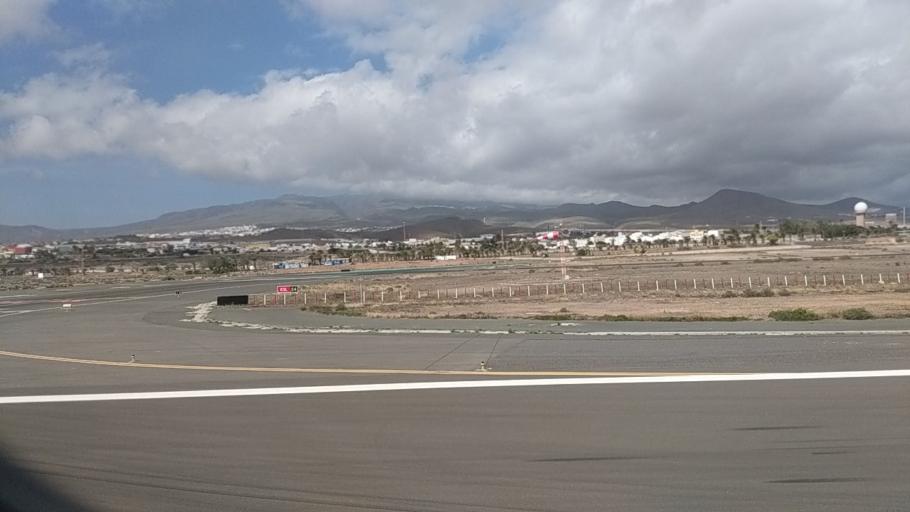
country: ES
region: Canary Islands
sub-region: Provincia de Las Palmas
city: Ingenio
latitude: 27.9187
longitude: -15.3900
